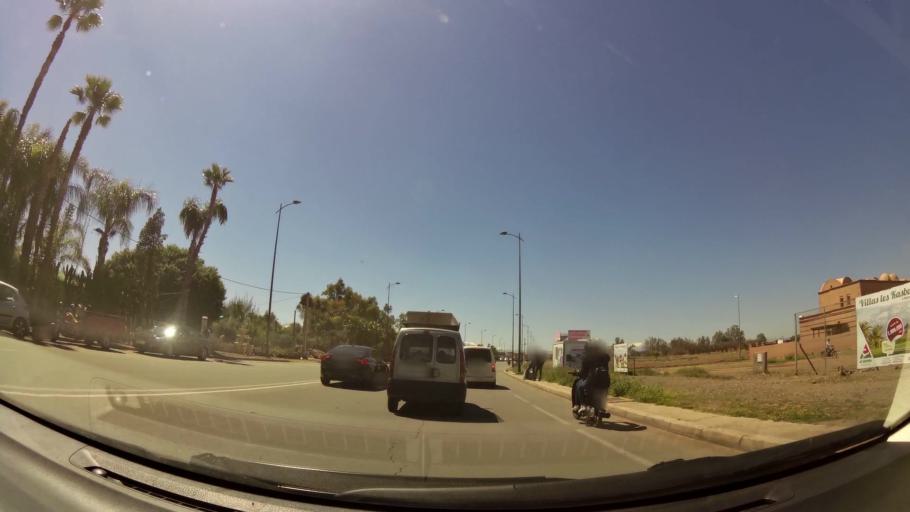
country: MA
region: Marrakech-Tensift-Al Haouz
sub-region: Marrakech
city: Marrakesh
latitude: 31.5703
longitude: -7.9803
